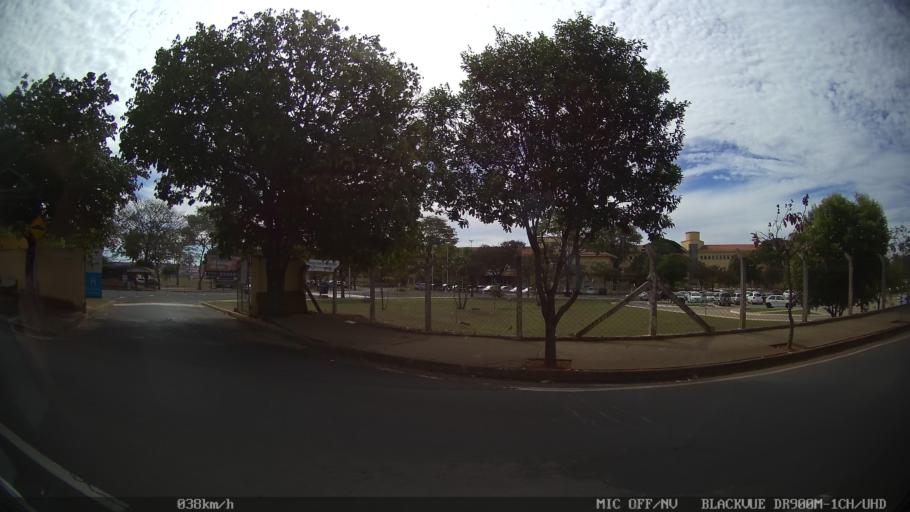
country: BR
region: Sao Paulo
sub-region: Catanduva
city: Catanduva
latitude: -21.1500
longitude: -48.9602
